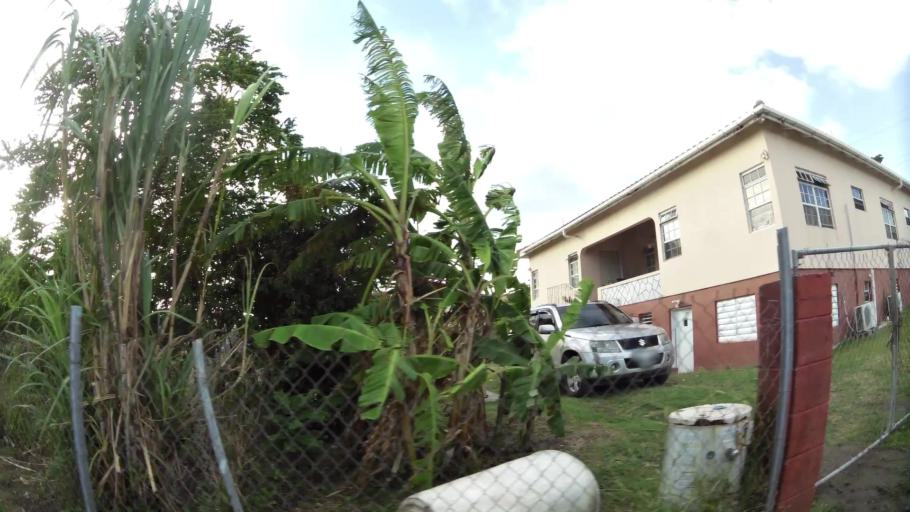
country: AG
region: Saint George
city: Piggotts
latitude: 17.1603
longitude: -61.8201
